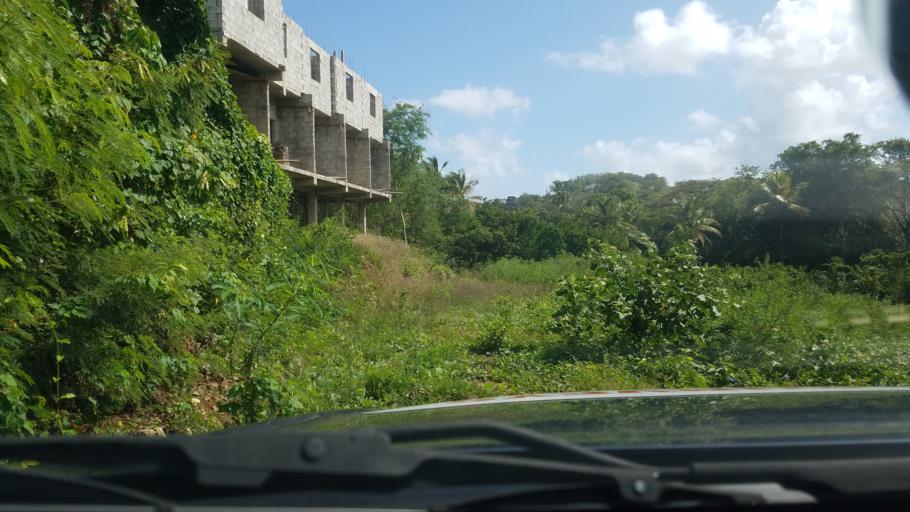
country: LC
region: Gros-Islet
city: Gros Islet
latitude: 14.0637
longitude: -60.9451
